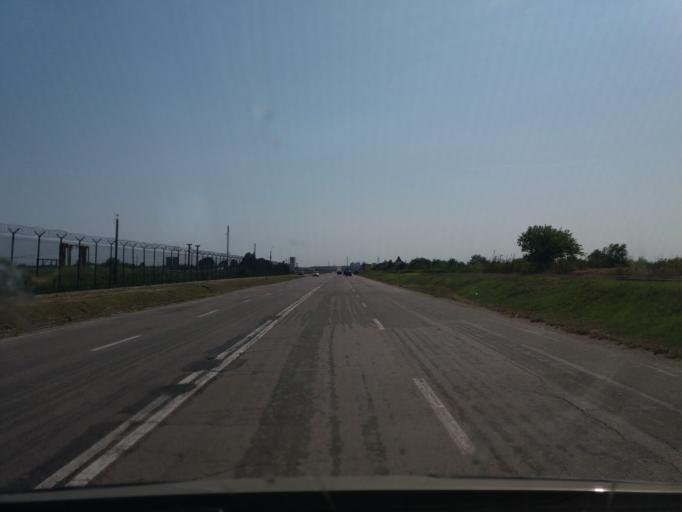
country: RO
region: Constanta
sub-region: Comuna Navodari
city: Navodari
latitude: 44.3401
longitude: 28.6380
